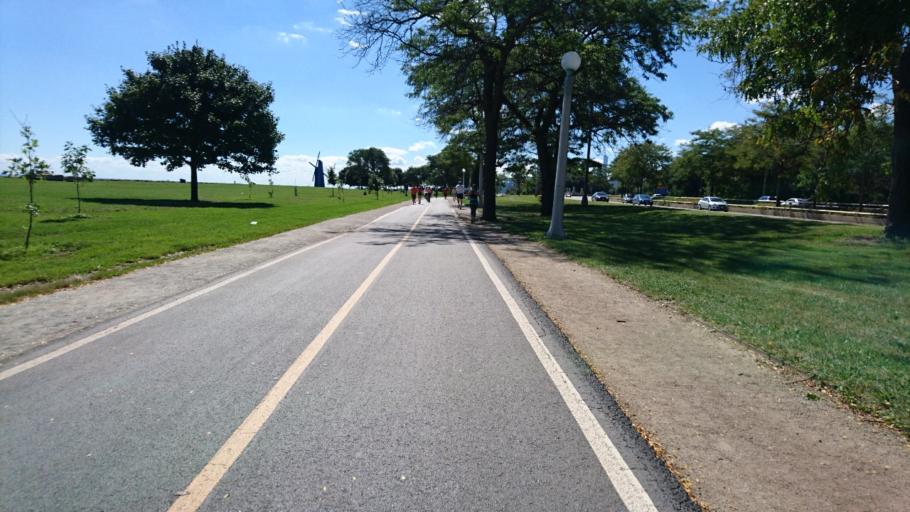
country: US
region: Illinois
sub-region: Cook County
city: Chicago
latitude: 41.9354
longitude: -87.6322
